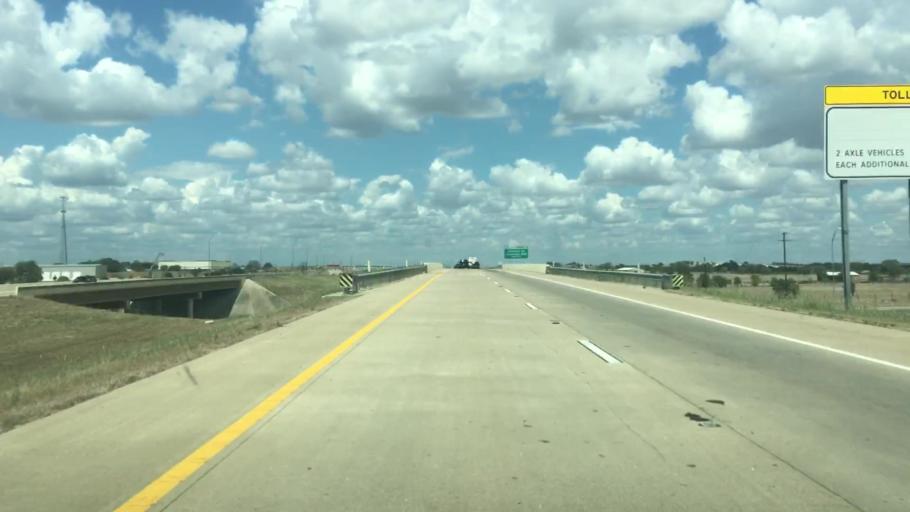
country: US
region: Texas
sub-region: Williamson County
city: Hutto
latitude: 30.5749
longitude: -97.5840
